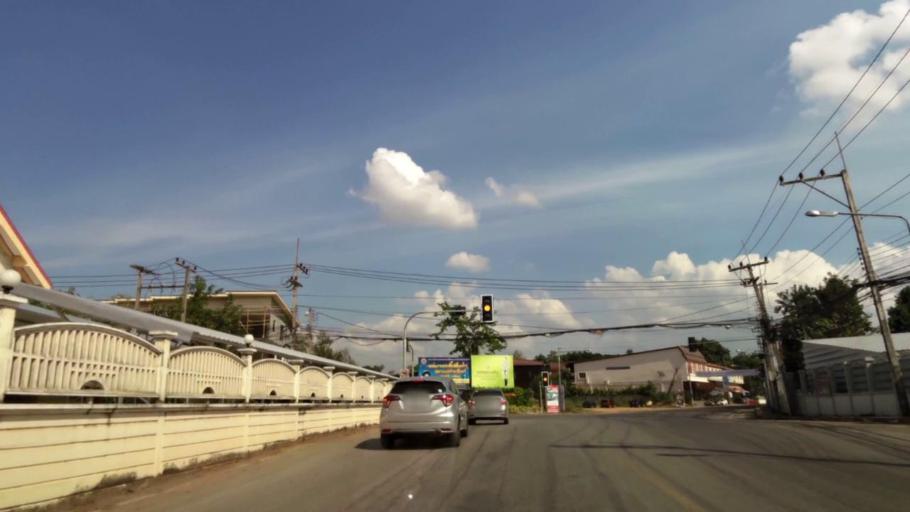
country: TH
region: Phrae
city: Phrae
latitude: 18.1358
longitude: 100.1341
